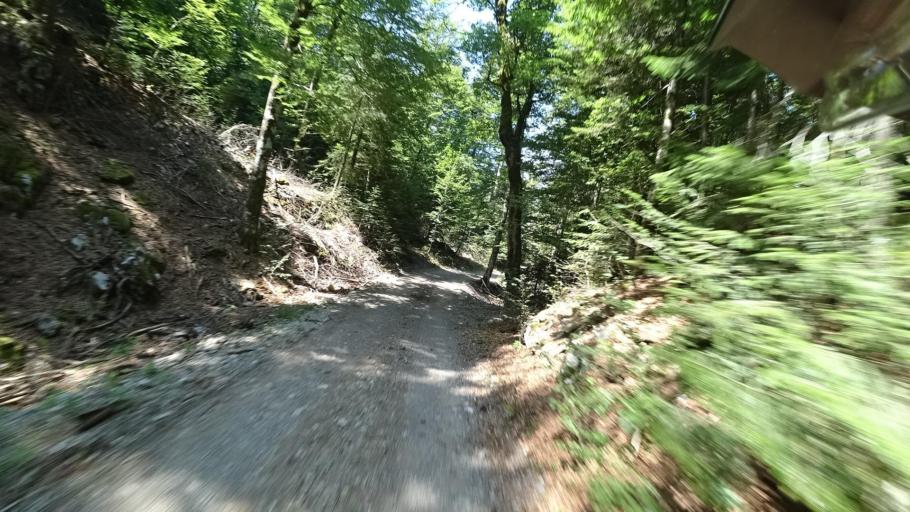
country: HR
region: Primorsko-Goranska
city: Bribir
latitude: 45.2576
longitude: 14.8973
